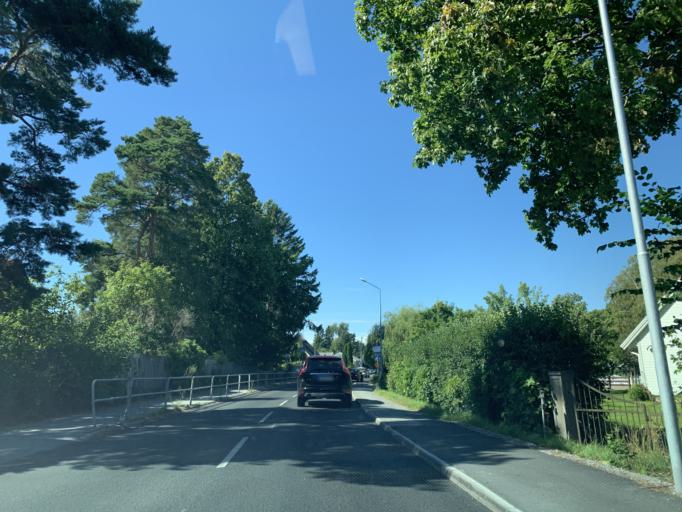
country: SE
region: Stockholm
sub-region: Ekero Kommun
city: Ekeroe
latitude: 59.2732
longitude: 17.7898
